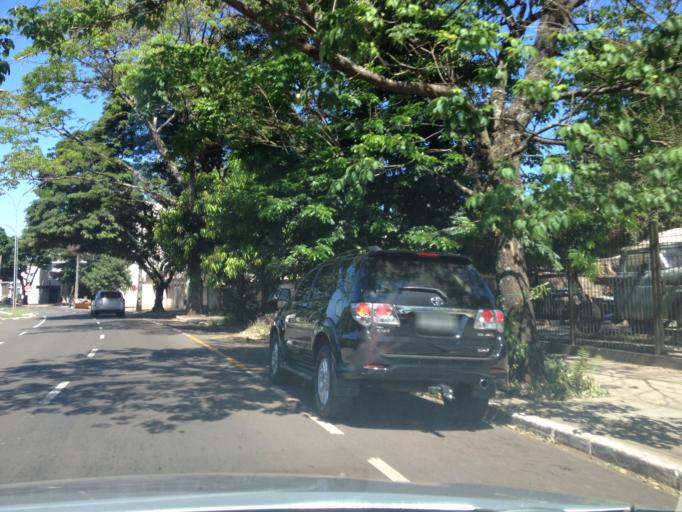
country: BR
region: Parana
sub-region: Maringa
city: Maringa
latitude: -23.4287
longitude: -51.9481
